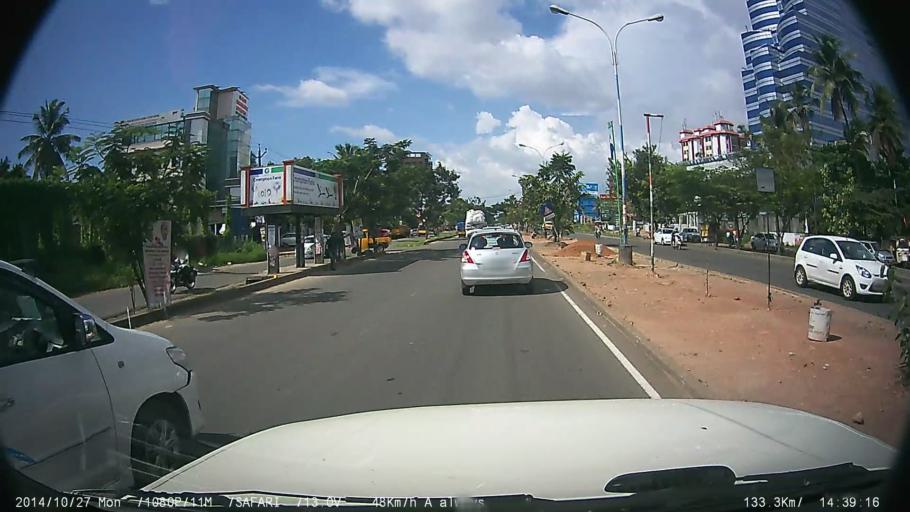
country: IN
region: Kerala
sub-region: Ernakulam
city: Cochin
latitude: 9.9890
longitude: 76.3156
